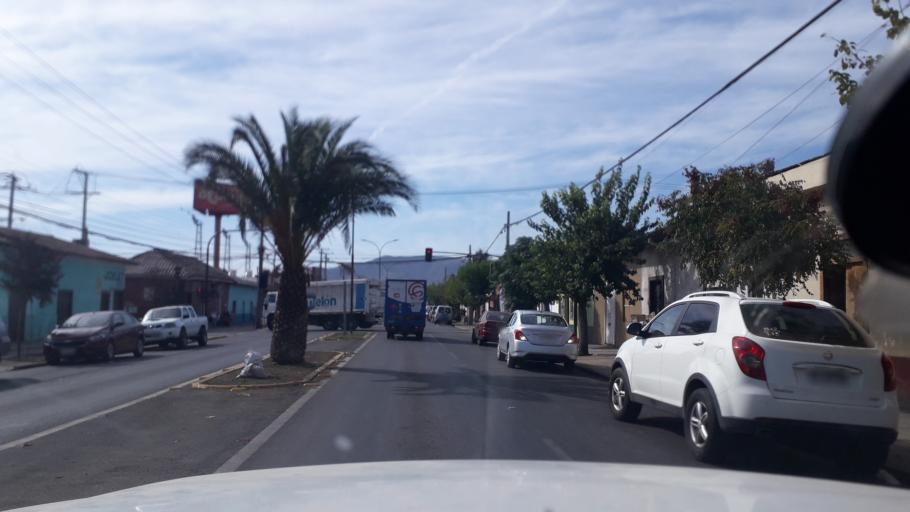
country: CL
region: Valparaiso
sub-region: Provincia de San Felipe
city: San Felipe
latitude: -32.7495
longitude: -70.7298
